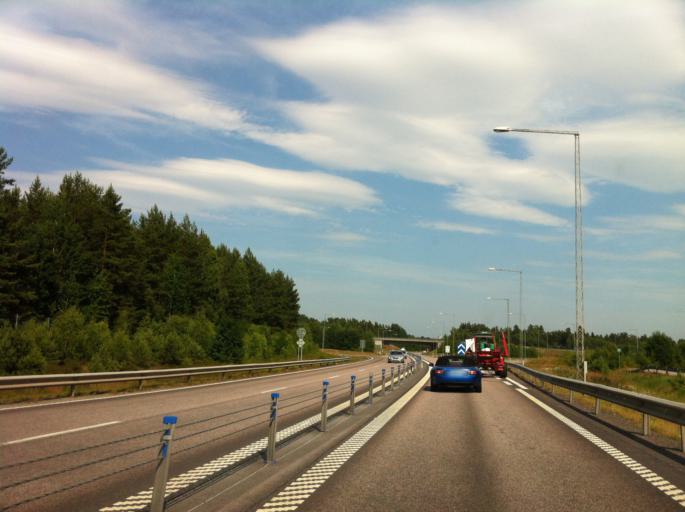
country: SE
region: Kalmar
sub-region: Kalmar Kommun
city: Trekanten
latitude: 56.6890
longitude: 16.1165
